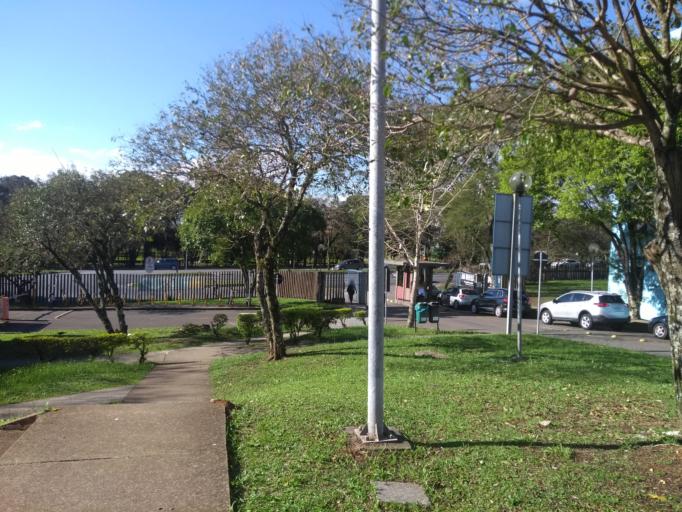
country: BR
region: Parana
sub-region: Curitiba
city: Curitiba
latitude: -25.4447
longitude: -49.2388
